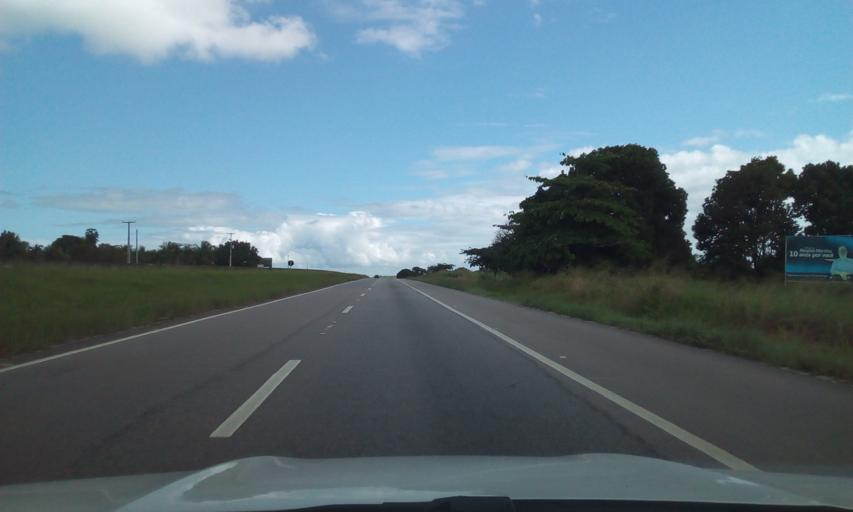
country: BR
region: Pernambuco
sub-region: Itapissuma
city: Itapissuma
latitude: -7.7035
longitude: -34.9247
